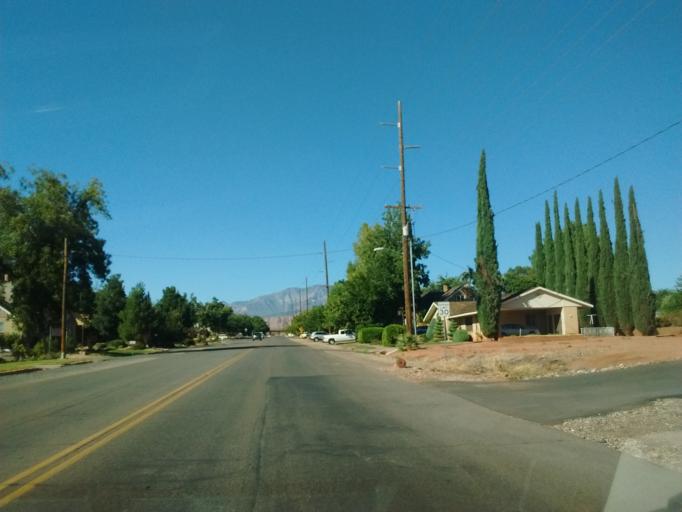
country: US
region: Utah
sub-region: Washington County
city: Washington
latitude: 37.1320
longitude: -113.5098
